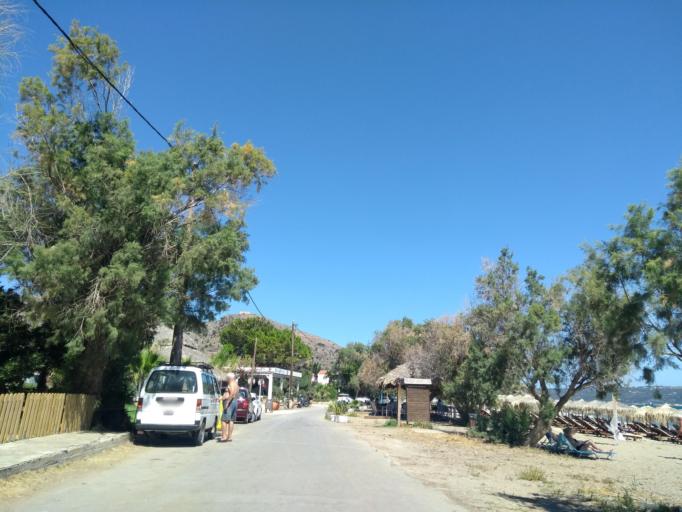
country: GR
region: Crete
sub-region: Nomos Chanias
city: Kalivai
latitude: 35.4606
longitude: 24.1618
